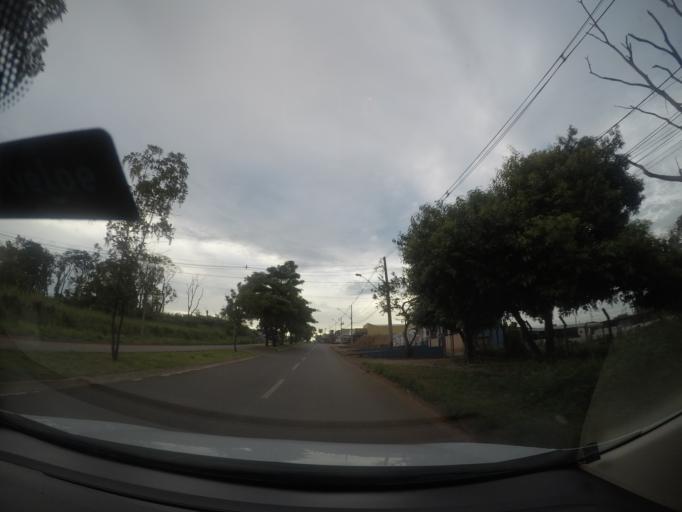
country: BR
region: Goias
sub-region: Goiania
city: Goiania
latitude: -16.7291
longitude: -49.3688
